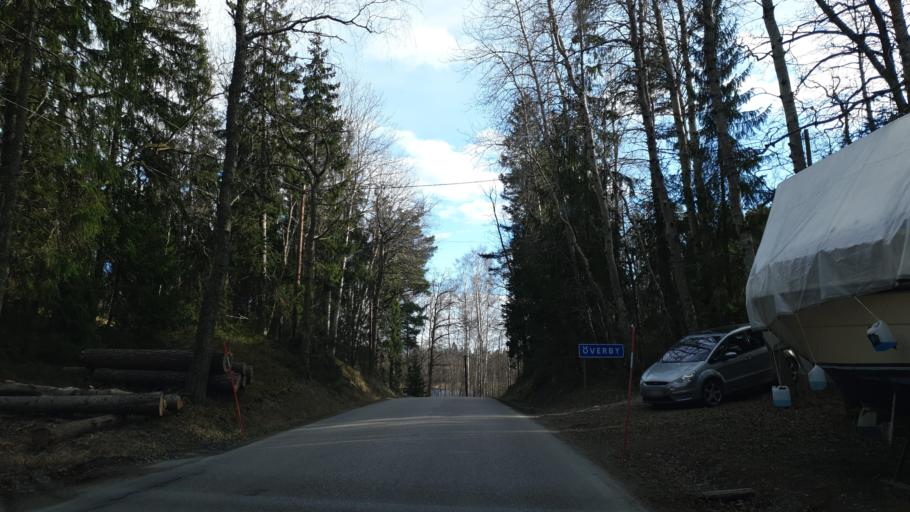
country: SE
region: Stockholm
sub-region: Varmdo Kommun
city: Holo
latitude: 59.3609
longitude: 18.6702
